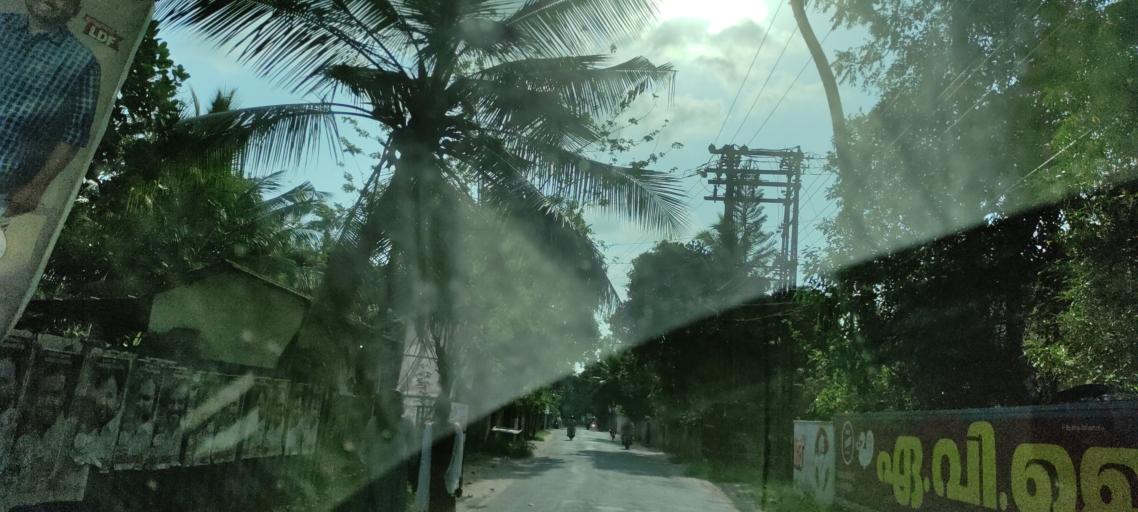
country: IN
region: Kerala
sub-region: Alappuzha
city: Vayalar
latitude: 9.6876
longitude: 76.3148
